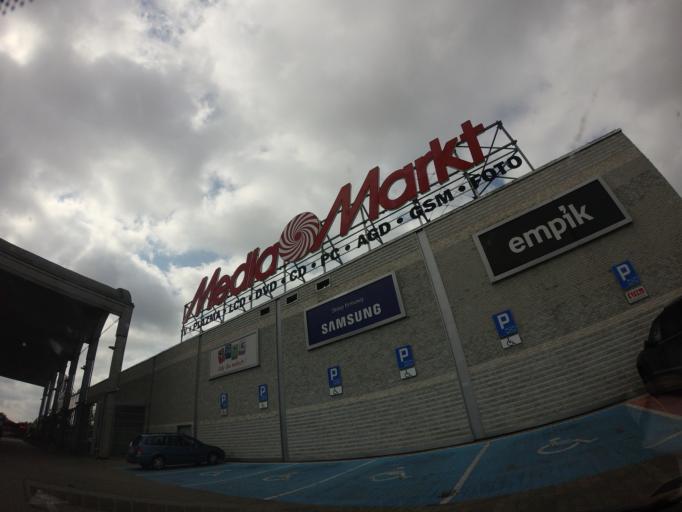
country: PL
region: Podlasie
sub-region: Bialystok
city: Bialystok
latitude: 53.1239
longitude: 23.1788
